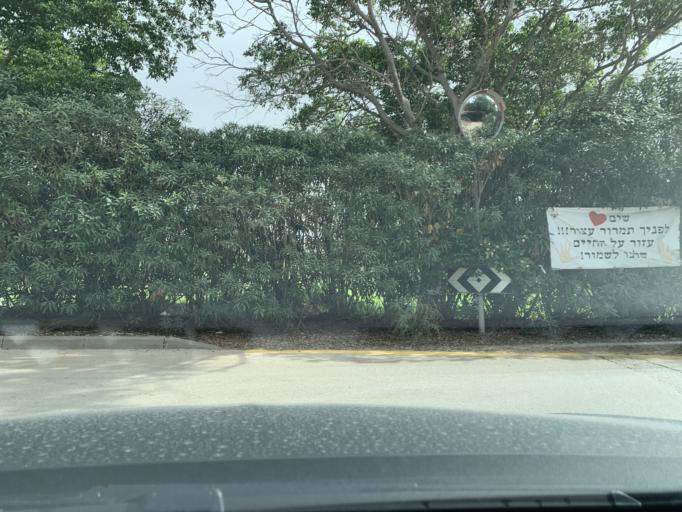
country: IL
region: Central District
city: Jaljulya
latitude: 32.1572
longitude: 34.9467
